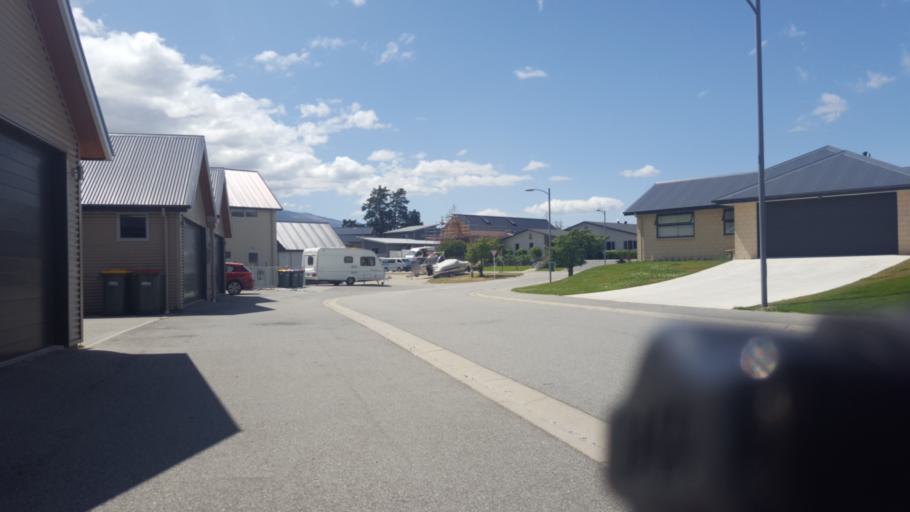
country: NZ
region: Otago
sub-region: Queenstown-Lakes District
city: Wanaka
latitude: -44.9805
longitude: 169.2373
